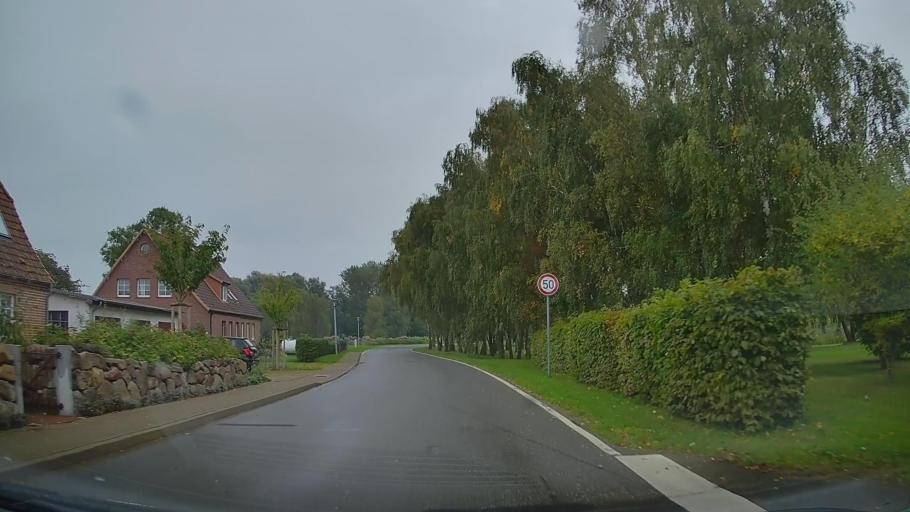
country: DE
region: Mecklenburg-Vorpommern
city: Kalkhorst
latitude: 54.0004
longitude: 11.0493
